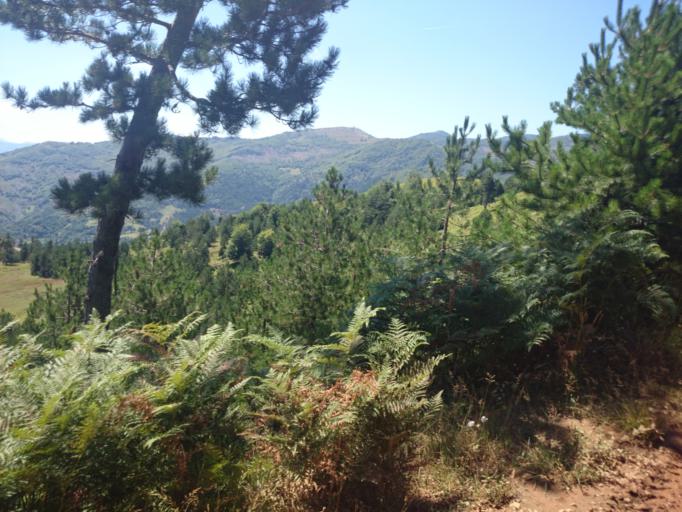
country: AL
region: Diber
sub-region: Rrethi i Bulqizes
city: Zerqan
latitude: 41.4491
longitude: 20.3507
